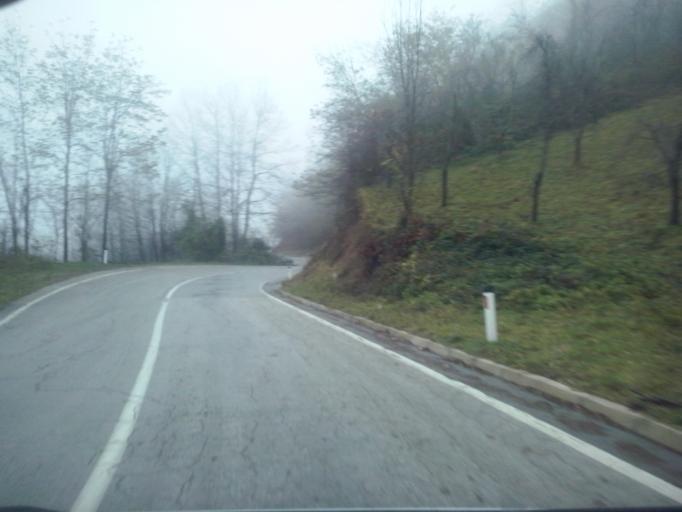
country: RS
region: Central Serbia
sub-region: Moravicki Okrug
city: Ivanjica
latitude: 43.5350
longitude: 20.2961
